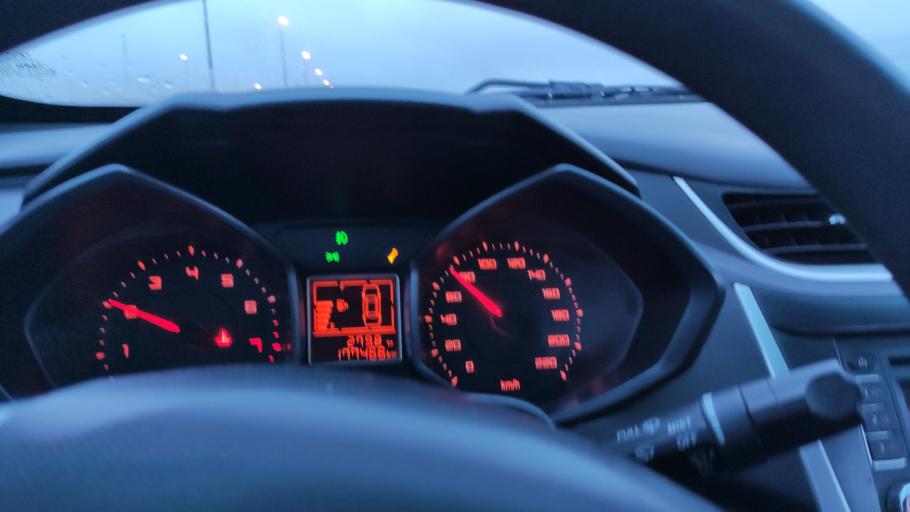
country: IR
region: Razavi Khorasan
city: Torqabeh
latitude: 36.0372
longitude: 59.1478
